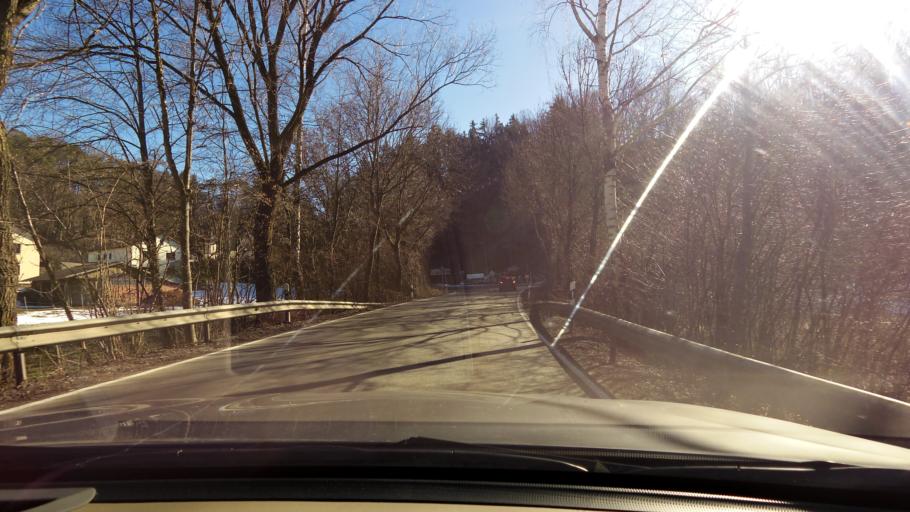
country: DE
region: Bavaria
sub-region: Upper Bavaria
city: Kraiburg am Inn
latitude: 48.1865
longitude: 12.4454
